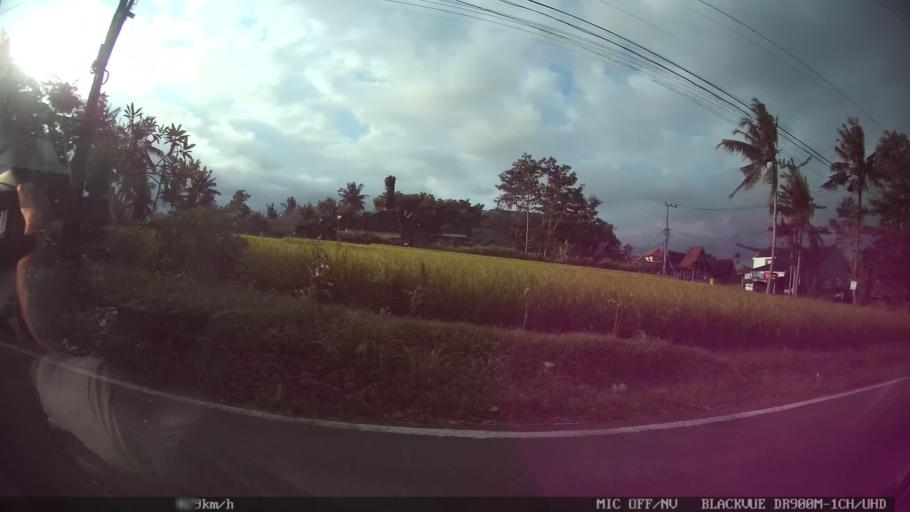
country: ID
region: Bali
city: Banjar Pande
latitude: -8.5158
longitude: 115.2503
